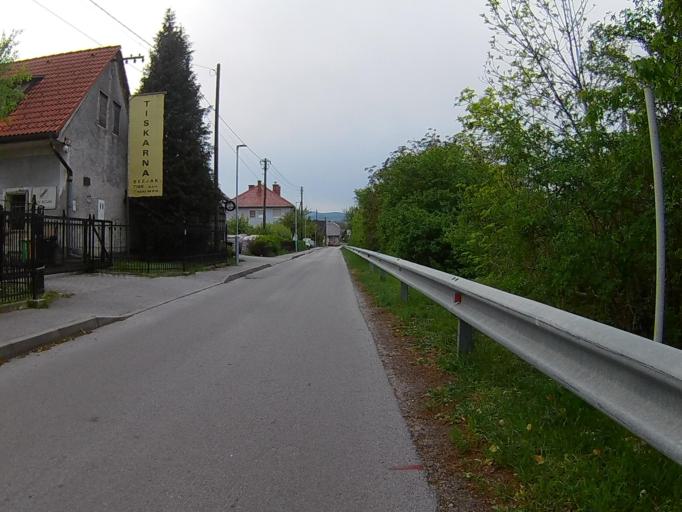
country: SI
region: Maribor
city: Kamnica
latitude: 46.5614
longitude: 15.6180
